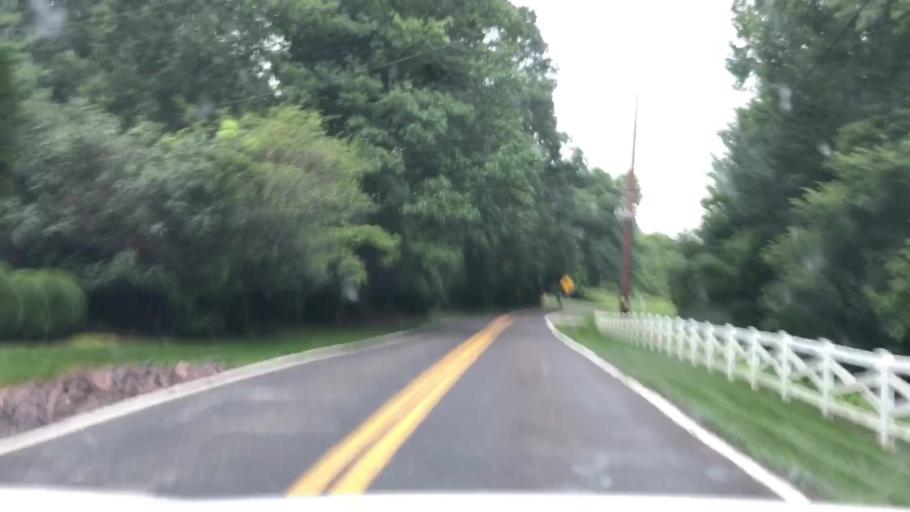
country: US
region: Missouri
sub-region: Saint Louis County
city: Clarkson Valley
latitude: 38.6352
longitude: -90.6056
